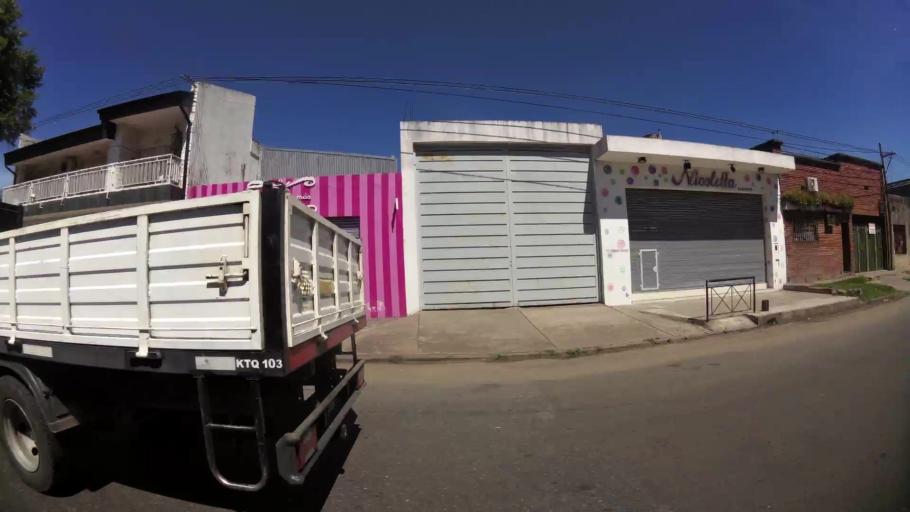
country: AR
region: Santa Fe
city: Perez
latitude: -32.9645
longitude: -60.7117
